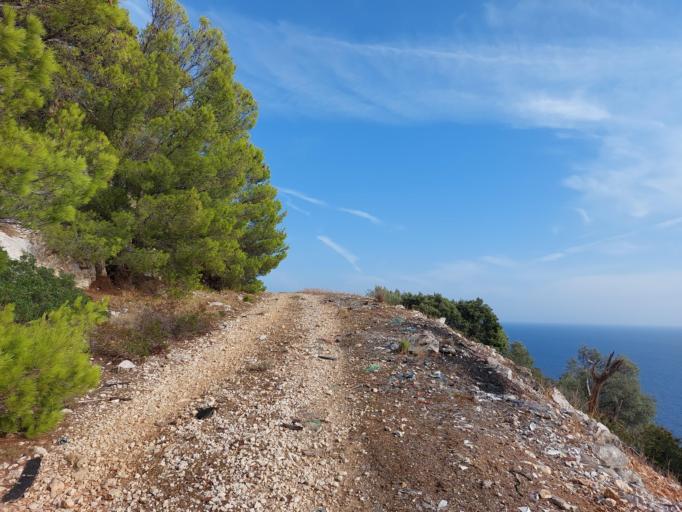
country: HR
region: Dubrovacko-Neretvanska
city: Smokvica
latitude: 42.7329
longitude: 16.8298
